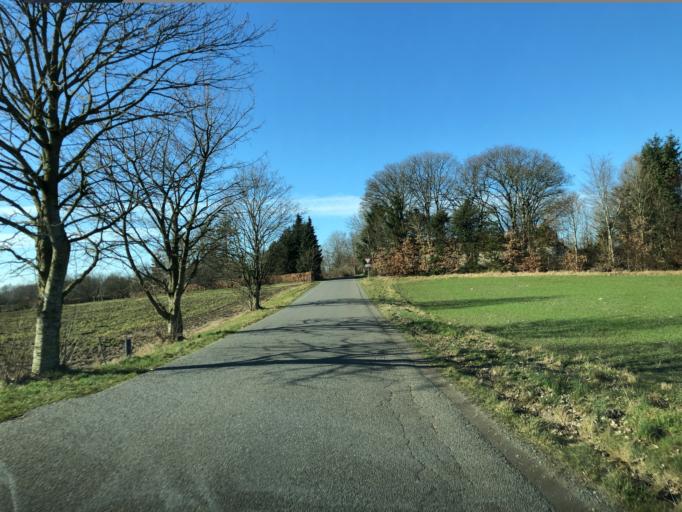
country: DK
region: Central Jutland
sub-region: Ikast-Brande Kommune
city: Bording Kirkeby
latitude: 56.1557
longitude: 9.2375
